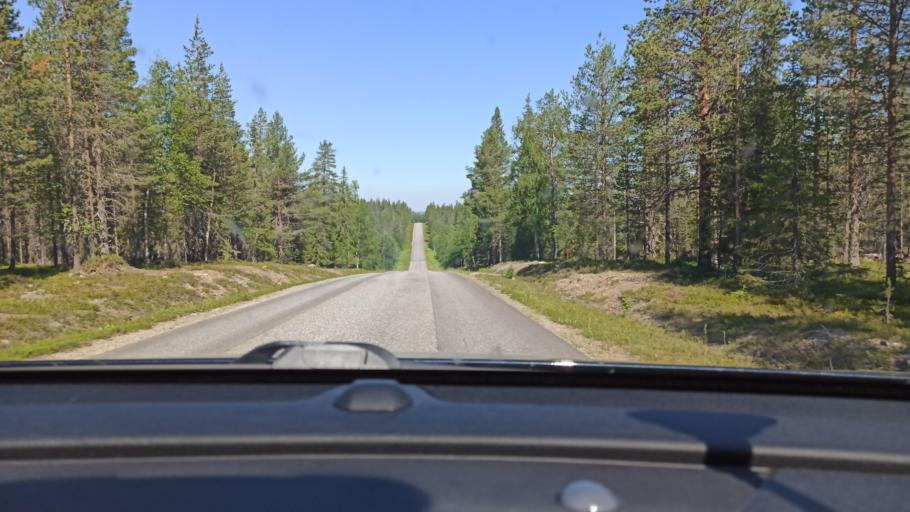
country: FI
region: Lapland
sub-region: Tunturi-Lappi
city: Kolari
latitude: 67.6758
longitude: 24.1440
